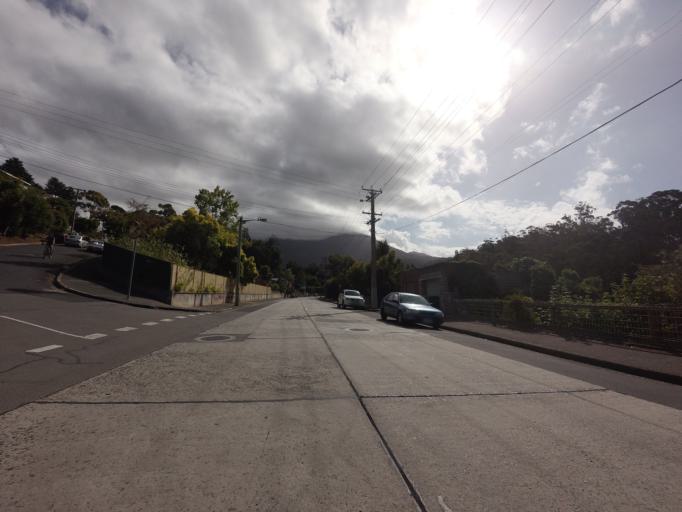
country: AU
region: Tasmania
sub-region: Hobart
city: Dynnyrne
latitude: -42.8957
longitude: 147.2965
